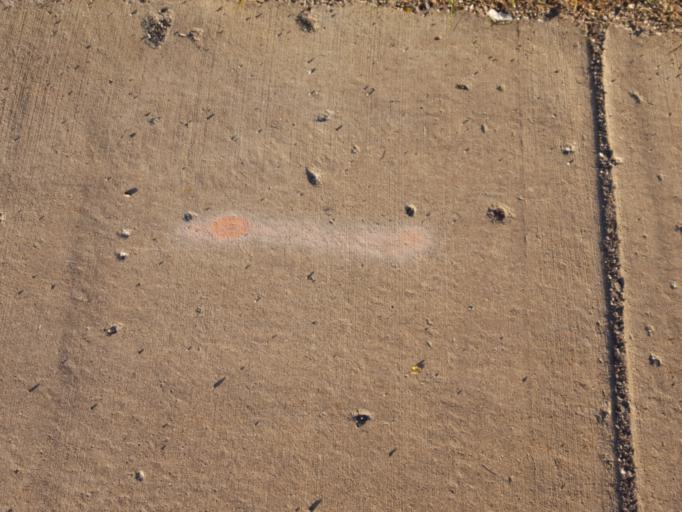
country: US
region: Illinois
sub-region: Cook County
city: Northbrook
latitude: 42.1483
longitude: -87.8323
